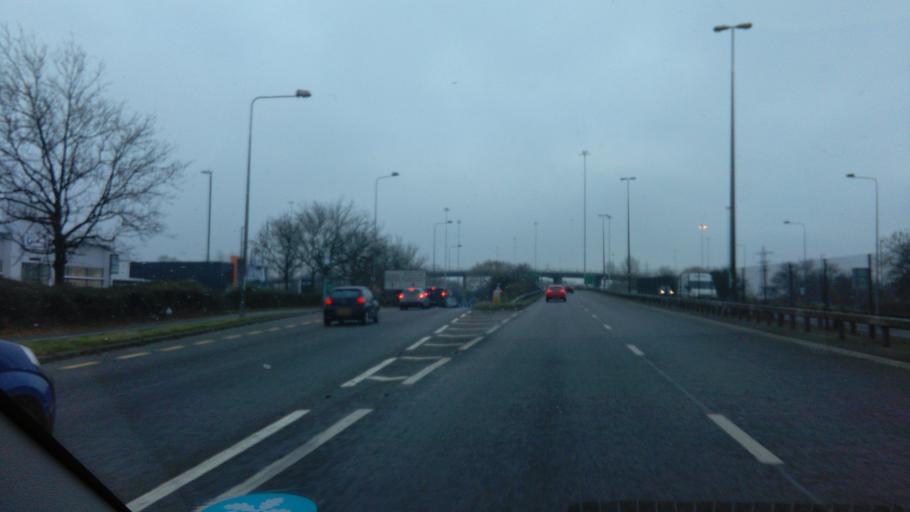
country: GB
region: England
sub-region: Nottingham
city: Nottingham
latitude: 52.9314
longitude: -1.1704
